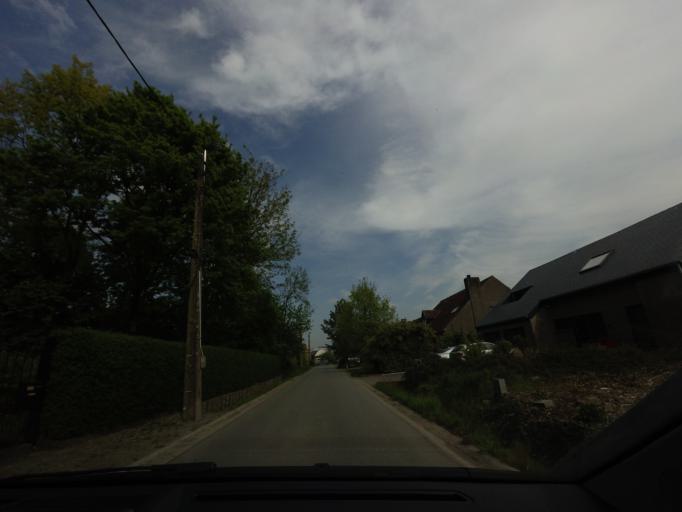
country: BE
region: Flanders
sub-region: Provincie Antwerpen
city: Kontich
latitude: 51.1078
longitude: 4.4668
